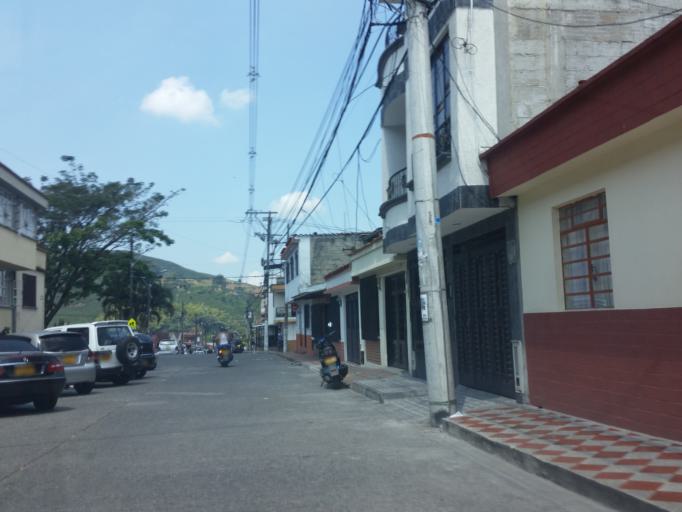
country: CO
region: Caldas
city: Chinchina
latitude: 4.9843
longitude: -75.6102
